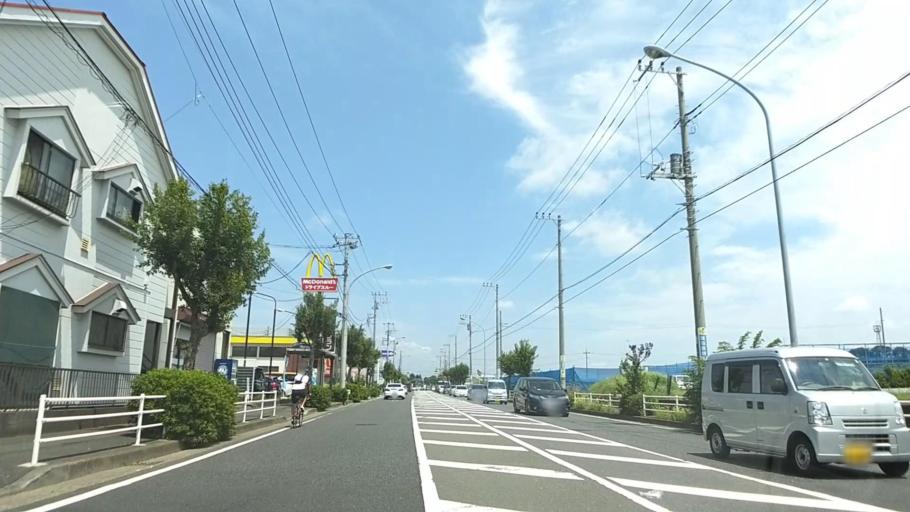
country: JP
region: Kanagawa
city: Minami-rinkan
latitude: 35.4464
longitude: 139.4841
